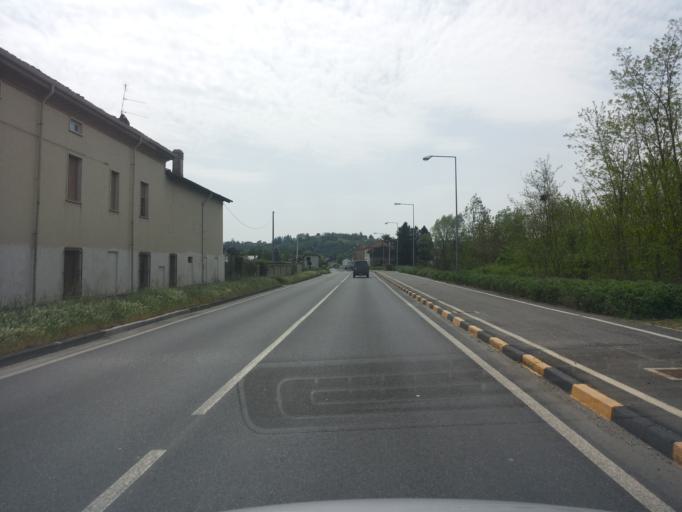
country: IT
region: Piedmont
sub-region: Provincia di Alessandria
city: Casale Monferrato
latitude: 45.1072
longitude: 8.4519
